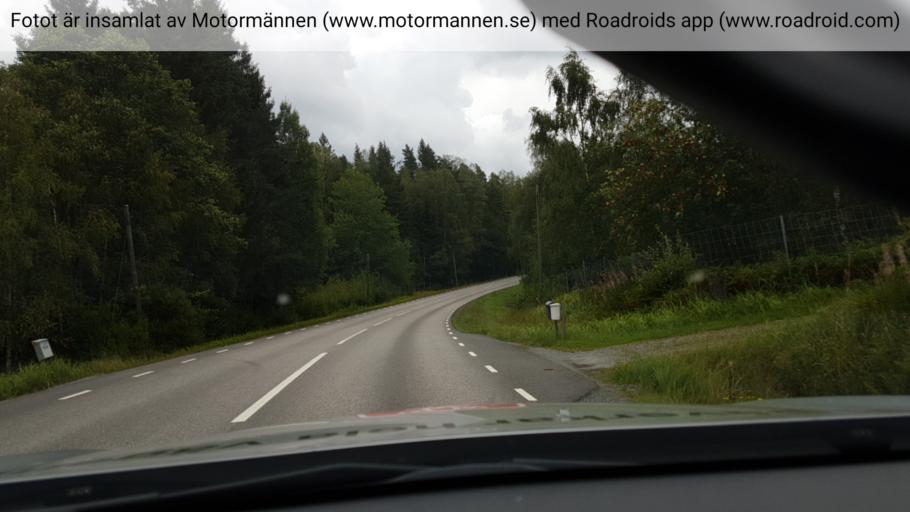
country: SE
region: Vaestra Goetaland
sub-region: Marks Kommun
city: Kinna
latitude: 57.4708
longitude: 12.7330
